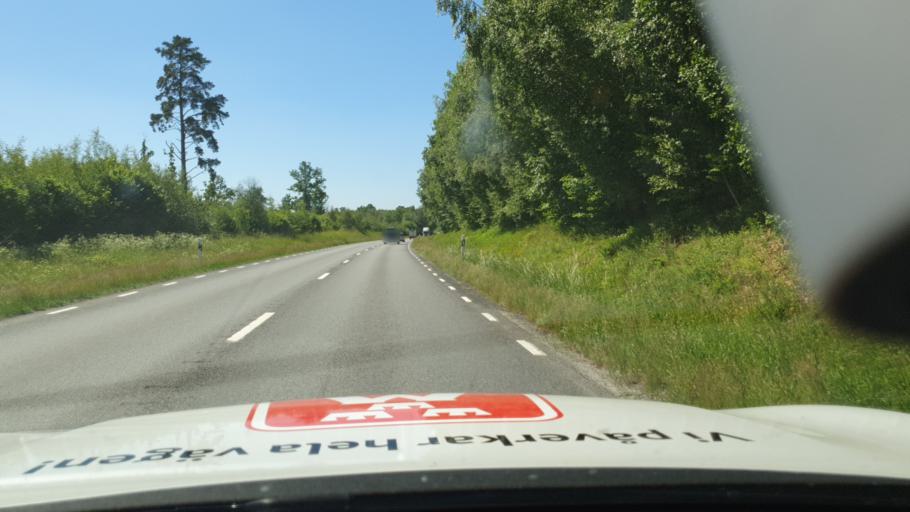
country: SE
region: Vaestra Goetaland
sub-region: Hjo Kommun
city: Hjo
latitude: 58.1220
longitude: 14.2168
